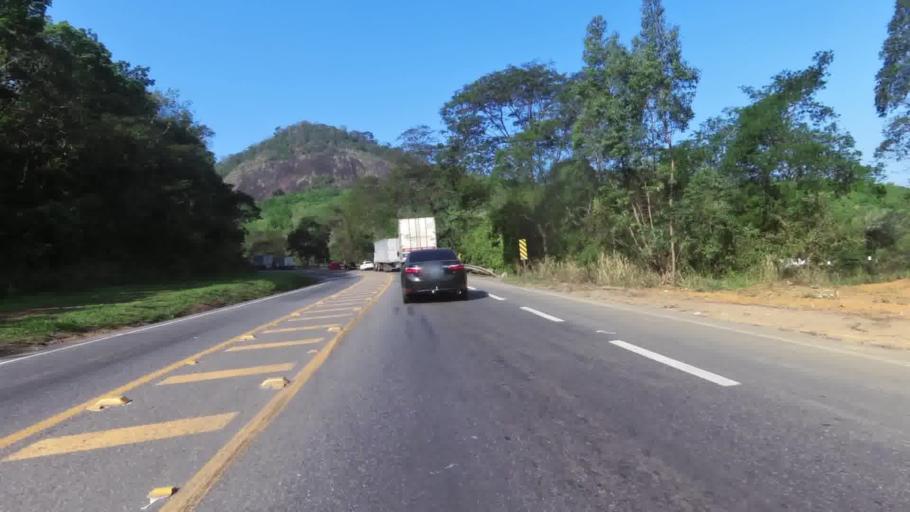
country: BR
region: Espirito Santo
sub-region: Alfredo Chaves
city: Alfredo Chaves
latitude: -20.7101
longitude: -40.7206
